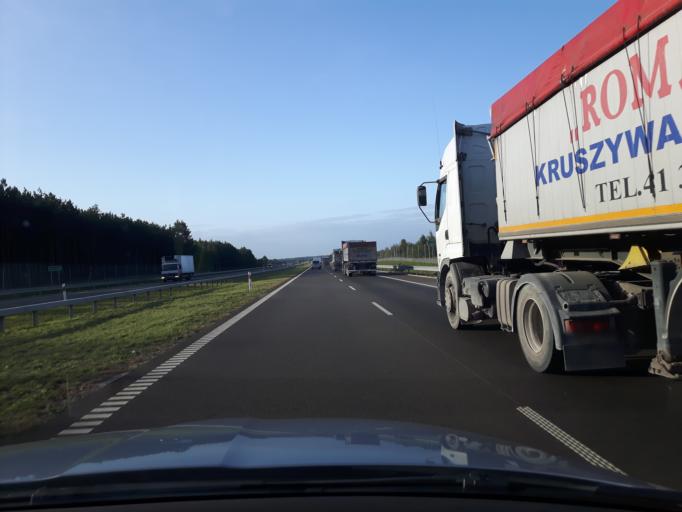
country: PL
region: Masovian Voivodeship
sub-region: Powiat radomski
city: Wolanow
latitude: 51.3767
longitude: 21.0183
